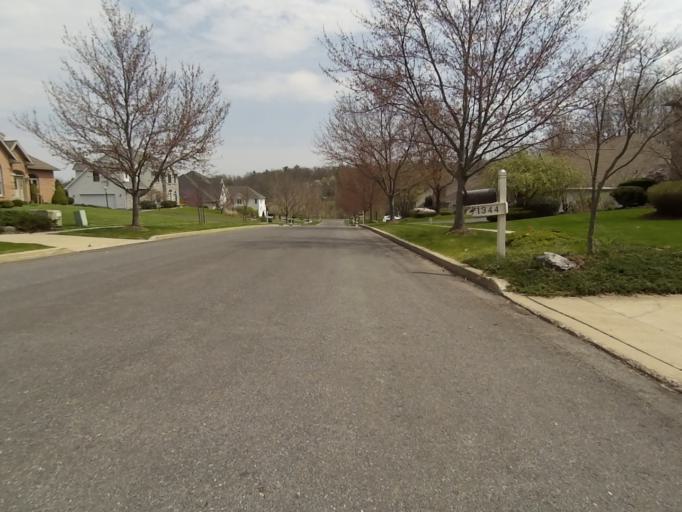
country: US
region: Pennsylvania
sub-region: Centre County
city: State College
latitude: 40.7946
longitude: -77.8870
